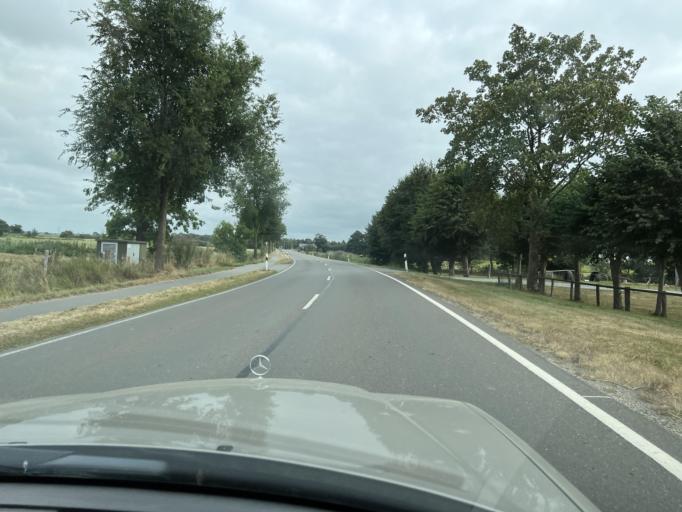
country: DE
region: Schleswig-Holstein
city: Stelle-Wittenwurth
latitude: 54.2620
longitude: 9.0529
